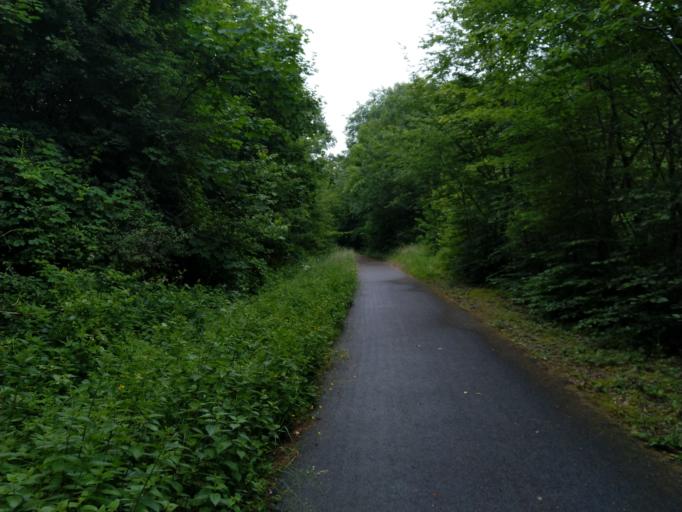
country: BE
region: Wallonia
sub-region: Province de Namur
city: Mettet
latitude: 50.3011
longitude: 4.7529
